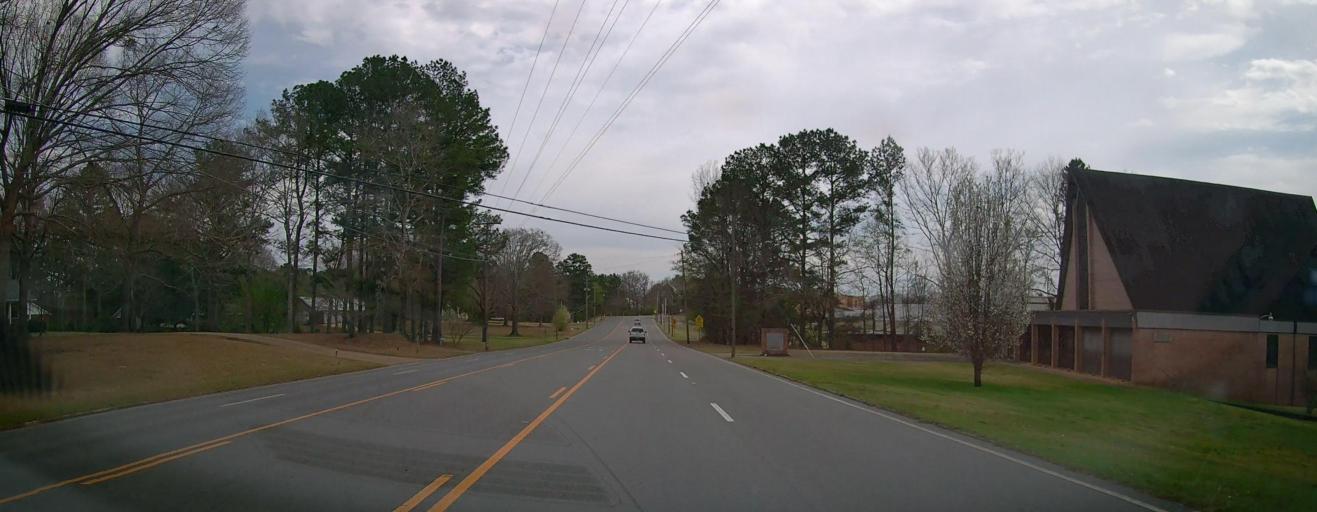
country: US
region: Alabama
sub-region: Marion County
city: Guin
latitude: 33.9772
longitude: -87.9167
